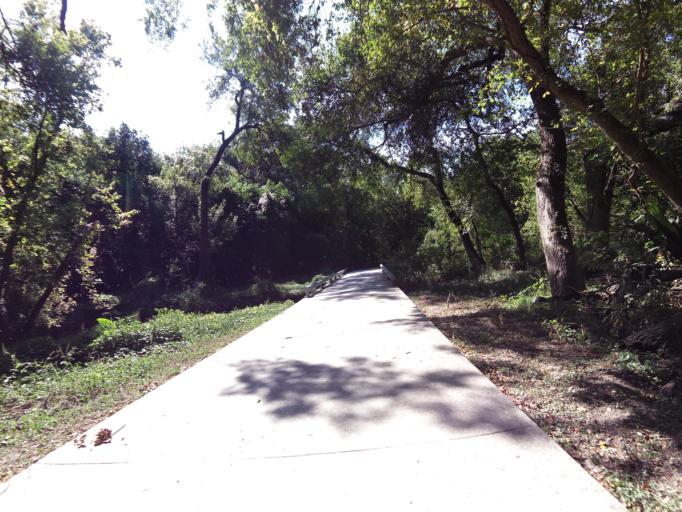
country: US
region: Texas
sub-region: Bexar County
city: China Grove
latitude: 29.3937
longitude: -98.4142
